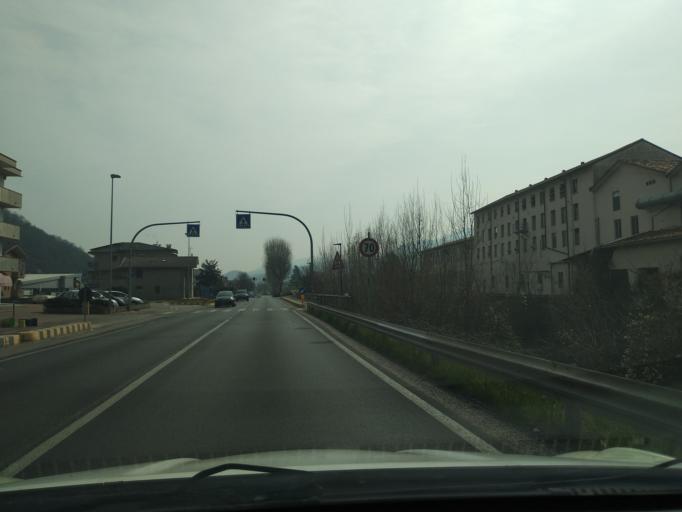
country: IT
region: Veneto
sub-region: Provincia di Vicenza
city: Chiampo
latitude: 45.5515
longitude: 11.2752
